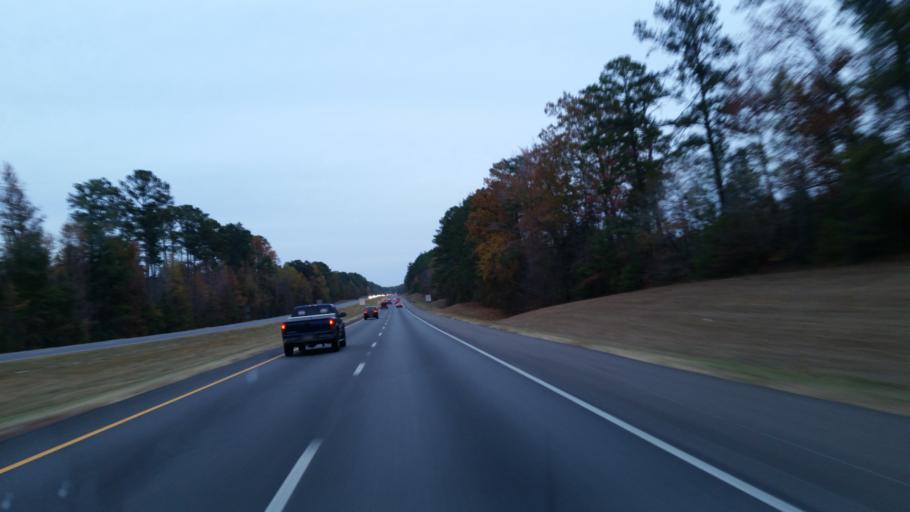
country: US
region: Alabama
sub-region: Greene County
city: Eutaw
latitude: 32.8816
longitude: -87.9085
